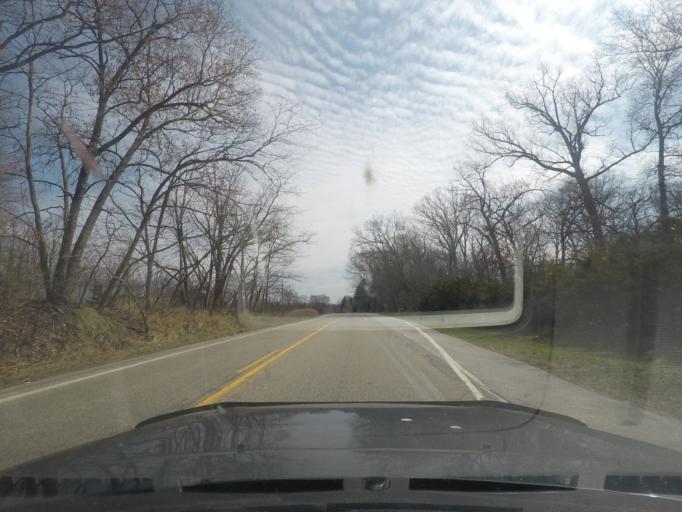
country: US
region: Indiana
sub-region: LaPorte County
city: Trail Creek
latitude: 41.6854
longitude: -86.7959
